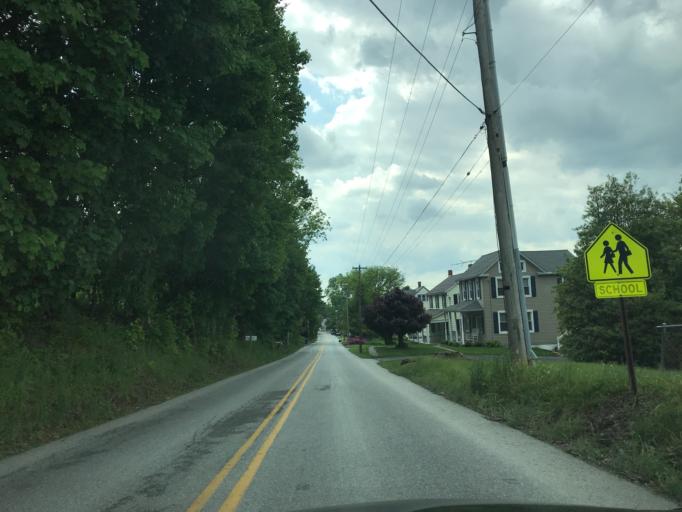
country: US
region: Pennsylvania
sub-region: York County
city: Susquehanna Trails
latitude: 39.7314
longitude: -76.3156
